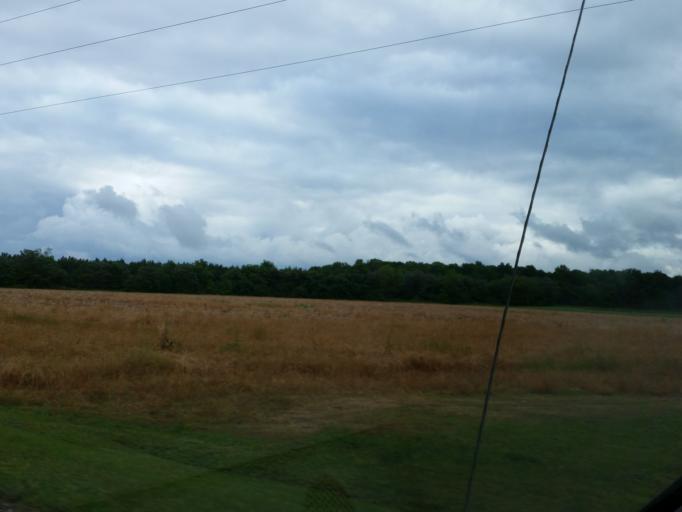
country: US
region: Georgia
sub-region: Peach County
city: Byron
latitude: 32.6671
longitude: -83.8694
